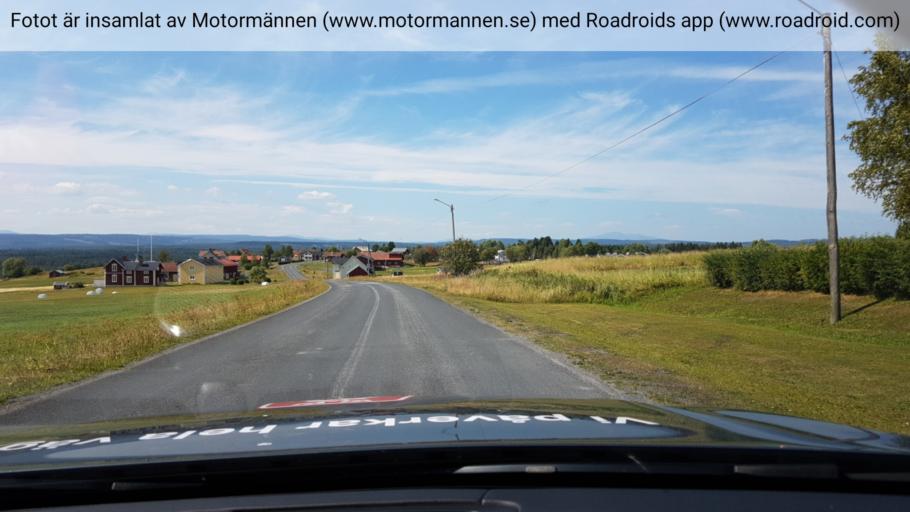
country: SE
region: Jaemtland
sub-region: Krokoms Kommun
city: Valla
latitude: 63.3036
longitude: 13.8799
